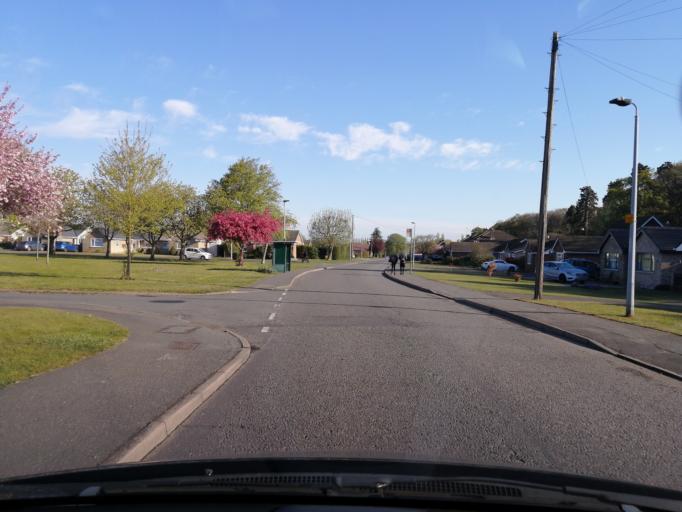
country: GB
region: England
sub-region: Cambridgeshire
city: Yaxley
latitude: 52.5508
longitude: -0.2897
